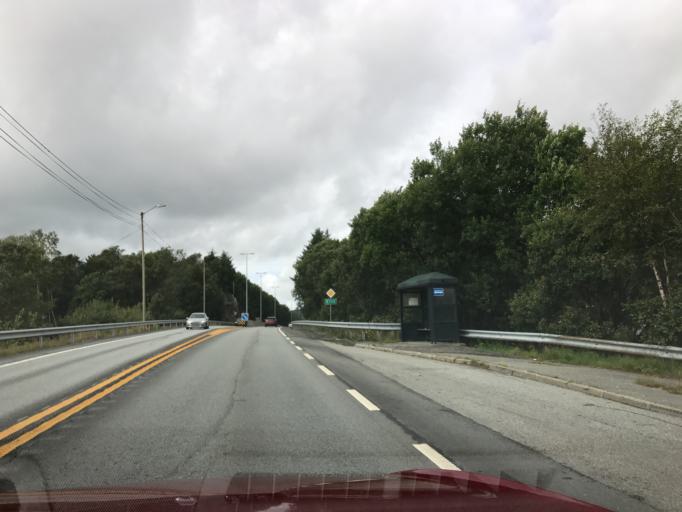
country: NO
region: Rogaland
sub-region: Karmoy
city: Eike
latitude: 59.4185
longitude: 5.4019
